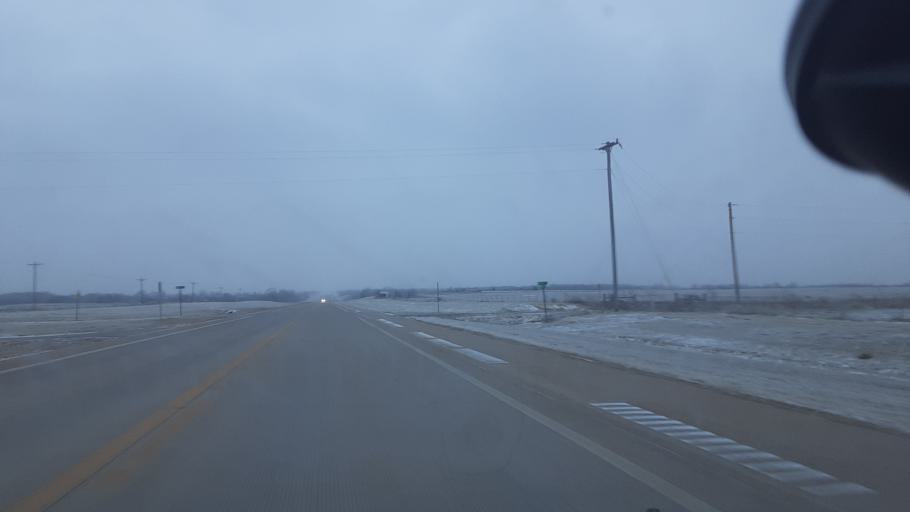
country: US
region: Oklahoma
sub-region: Payne County
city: Perkins
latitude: 35.9860
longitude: -97.1045
